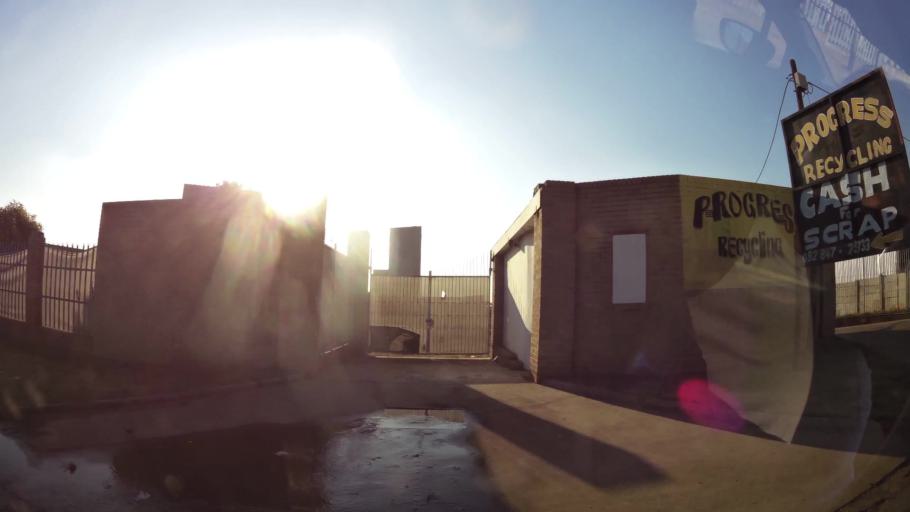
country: ZA
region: Gauteng
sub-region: West Rand District Municipality
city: Randfontein
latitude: -26.1913
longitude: 27.6911
